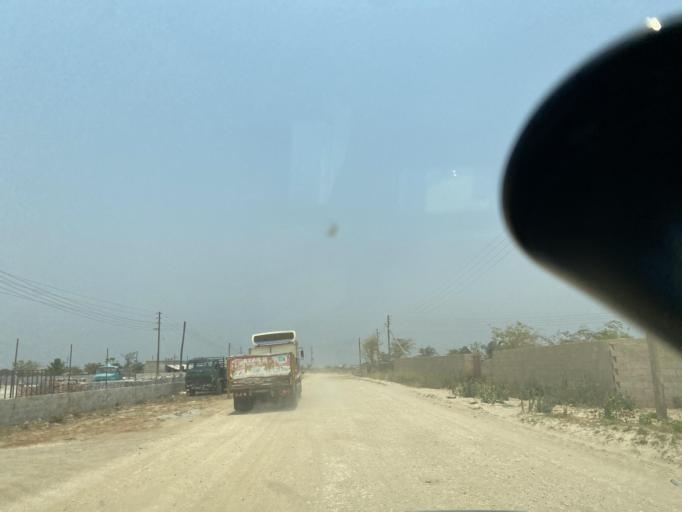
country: ZM
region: Lusaka
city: Lusaka
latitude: -15.5378
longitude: 28.3501
